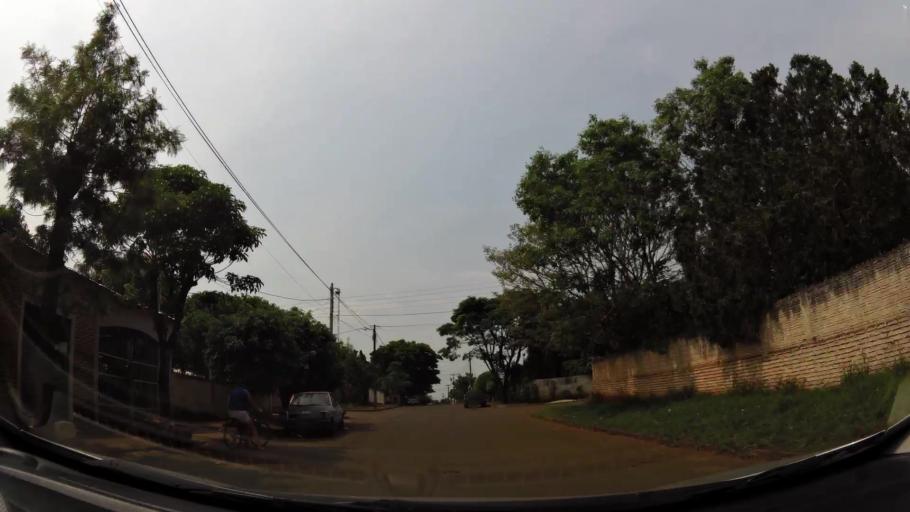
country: PY
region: Alto Parana
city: Presidente Franco
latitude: -25.5654
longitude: -54.6166
